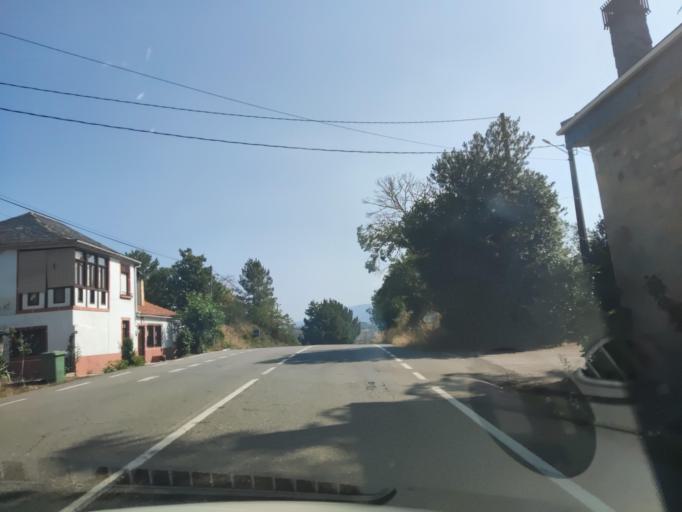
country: ES
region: Galicia
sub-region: Provincia de Ourense
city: Rios
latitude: 42.0269
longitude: -7.1838
